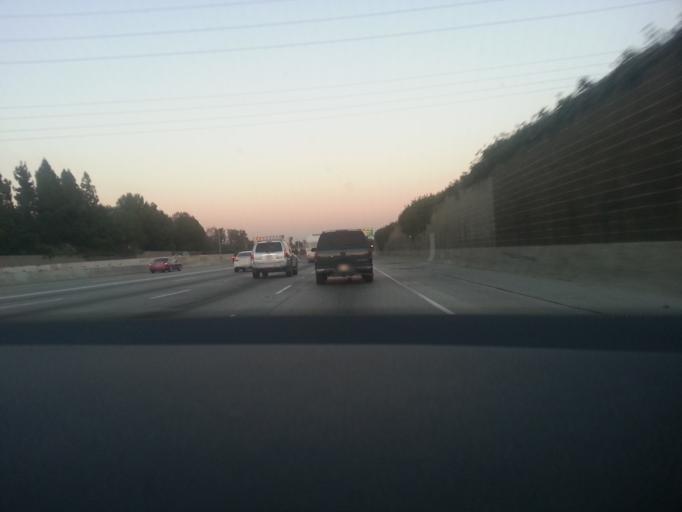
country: US
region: California
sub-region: Los Angeles County
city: Monterey Park
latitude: 34.0710
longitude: -118.1437
